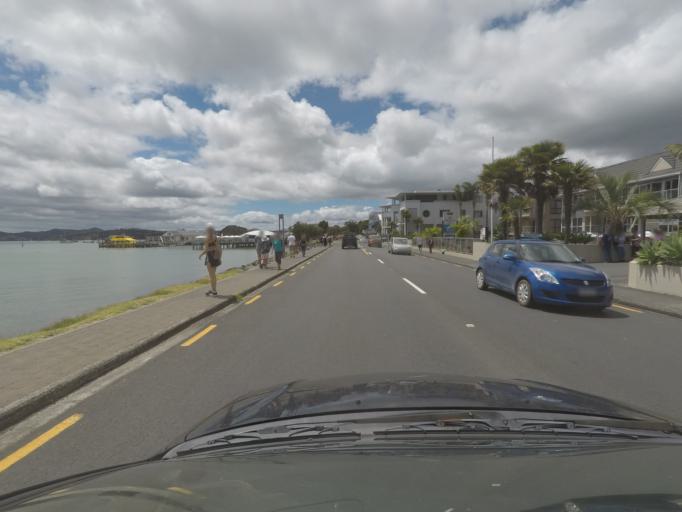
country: NZ
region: Northland
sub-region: Far North District
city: Paihia
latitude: -35.2801
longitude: 174.0903
